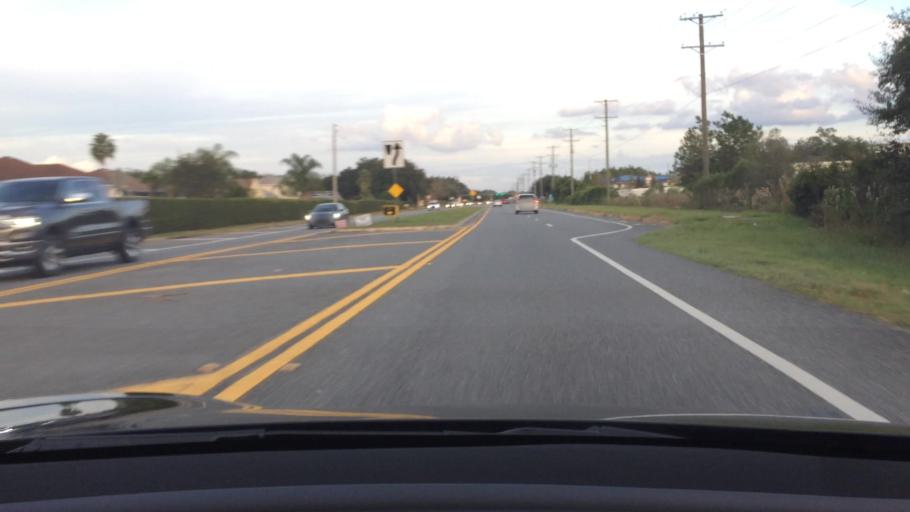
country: US
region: Florida
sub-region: Hillsborough County
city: Pebble Creek
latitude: 28.1712
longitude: -82.3597
